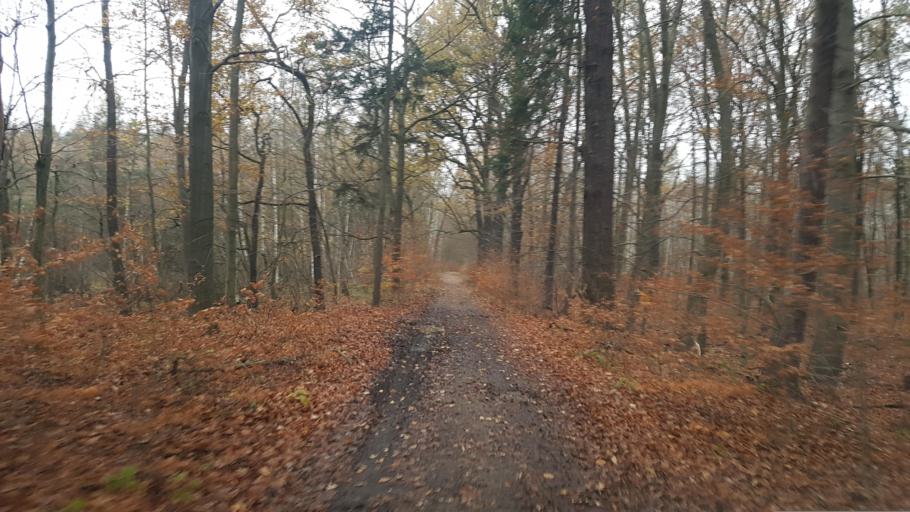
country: DE
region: Brandenburg
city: Crinitz
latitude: 51.7523
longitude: 13.7869
